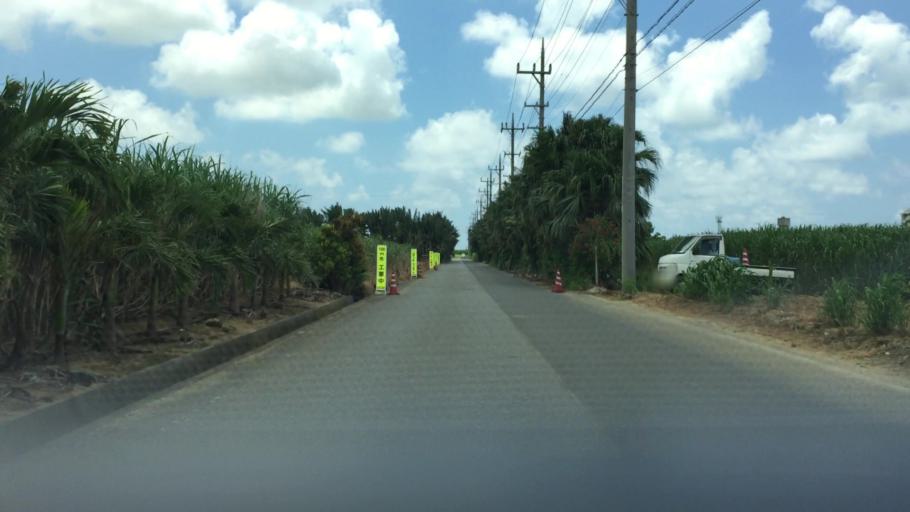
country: JP
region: Okinawa
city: Ishigaki
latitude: 24.3593
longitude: 124.1409
